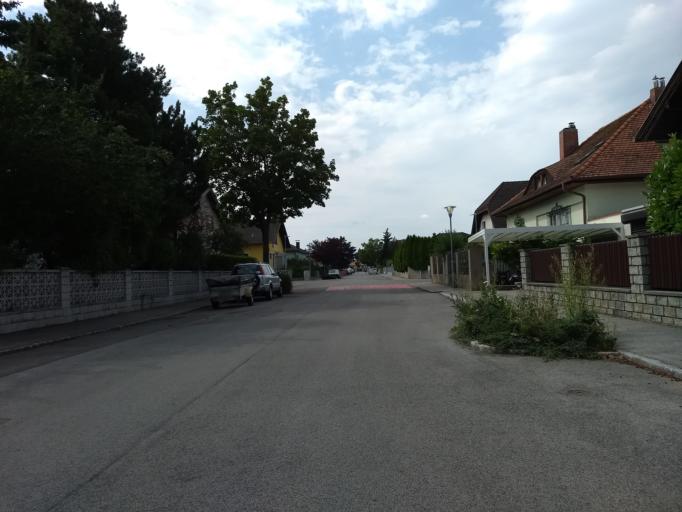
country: AT
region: Lower Austria
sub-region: Politischer Bezirk Modling
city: Neu-Guntramsdorf
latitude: 48.0566
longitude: 16.3203
